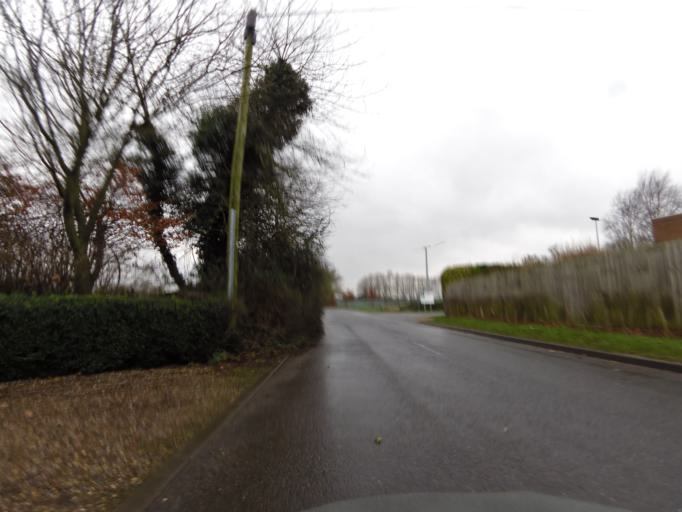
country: GB
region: England
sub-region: Norfolk
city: Briston
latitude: 52.7578
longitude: 1.1068
